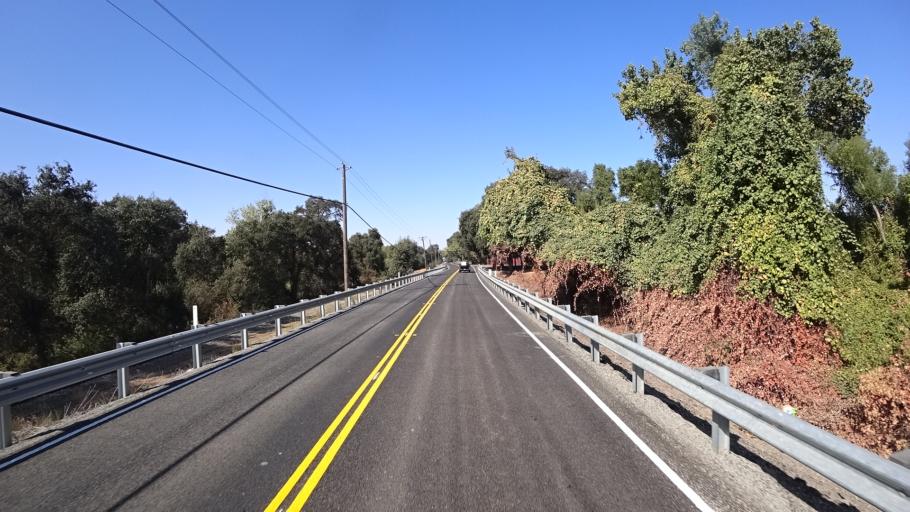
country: US
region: California
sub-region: Yolo County
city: West Sacramento
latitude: 38.6484
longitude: -121.6009
